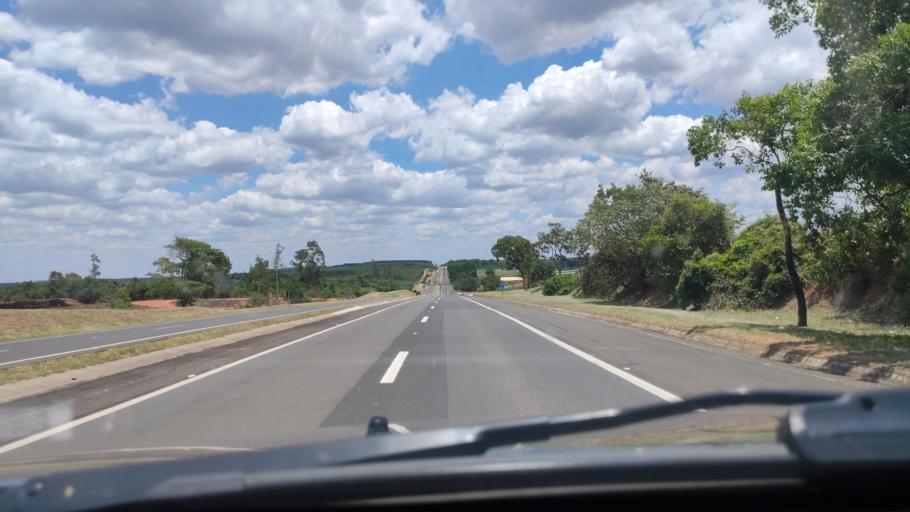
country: BR
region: Sao Paulo
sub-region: Duartina
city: Duartina
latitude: -22.5025
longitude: -49.2801
